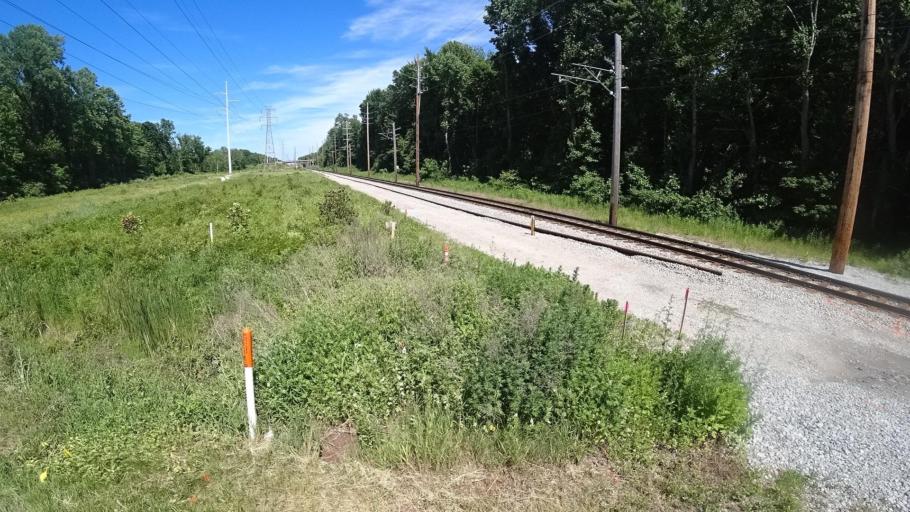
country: US
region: Indiana
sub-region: Porter County
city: Porter
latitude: 41.6427
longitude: -87.0673
